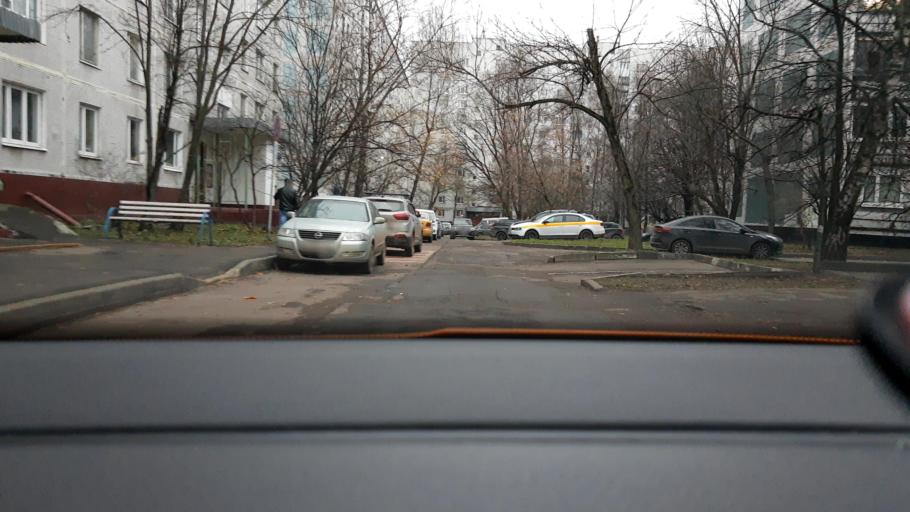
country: RU
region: Moscow
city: Bibirevo
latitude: 55.8962
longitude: 37.6279
